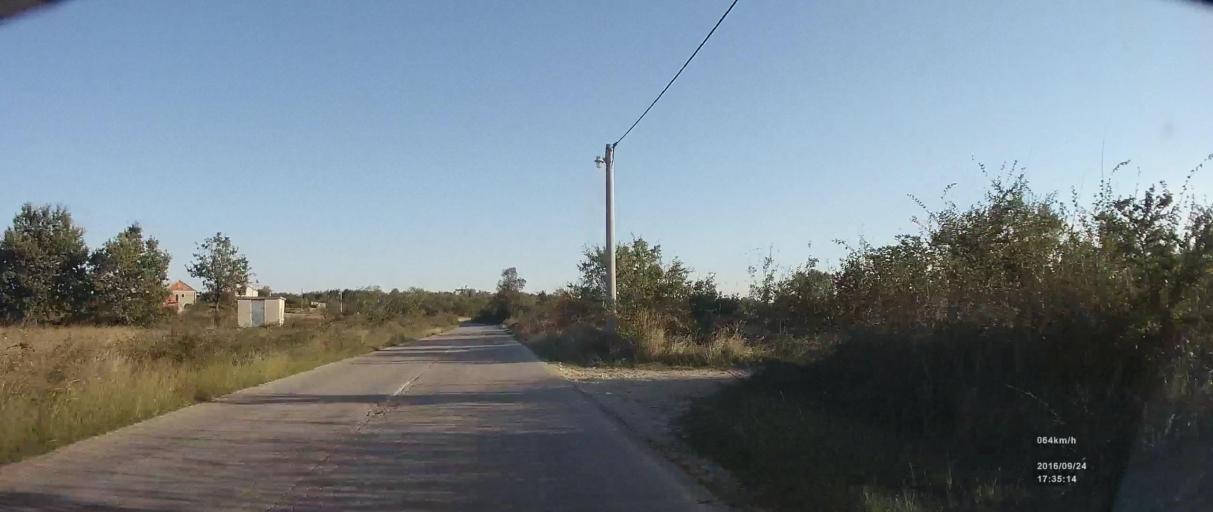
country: HR
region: Zadarska
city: Posedarje
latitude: 44.1618
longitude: 15.4656
